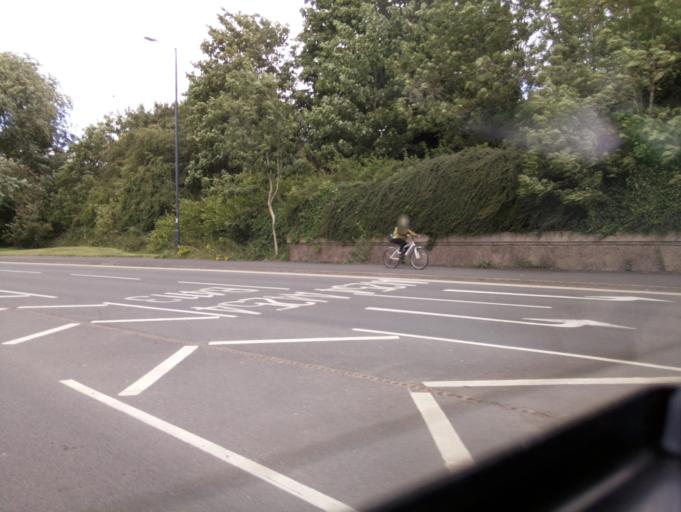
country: GB
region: England
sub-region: Warwickshire
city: Nuneaton
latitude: 52.5150
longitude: -1.4675
